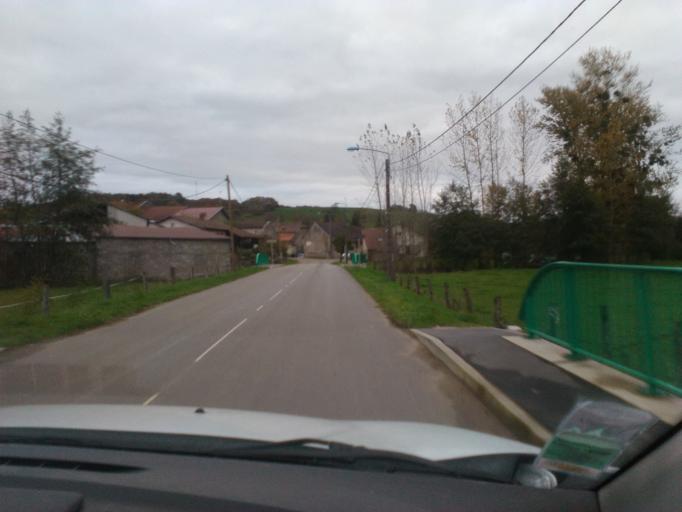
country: FR
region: Lorraine
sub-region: Departement des Vosges
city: Vincey
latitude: 48.2678
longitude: 6.2653
